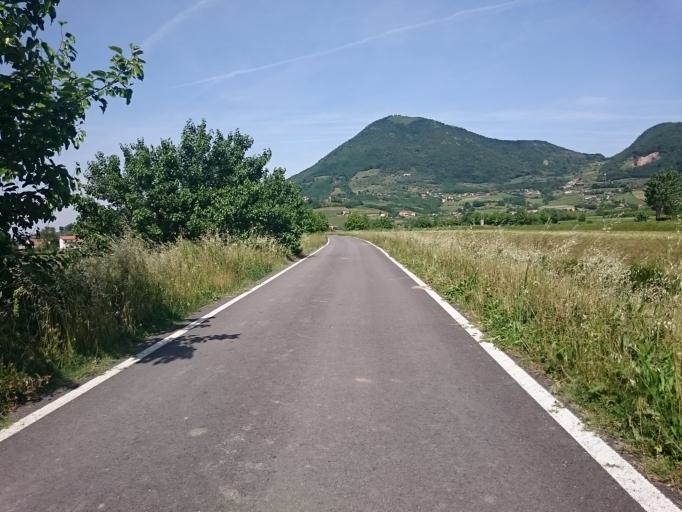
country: IT
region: Veneto
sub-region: Provincia di Padova
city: Vo
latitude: 45.3466
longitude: 11.6286
